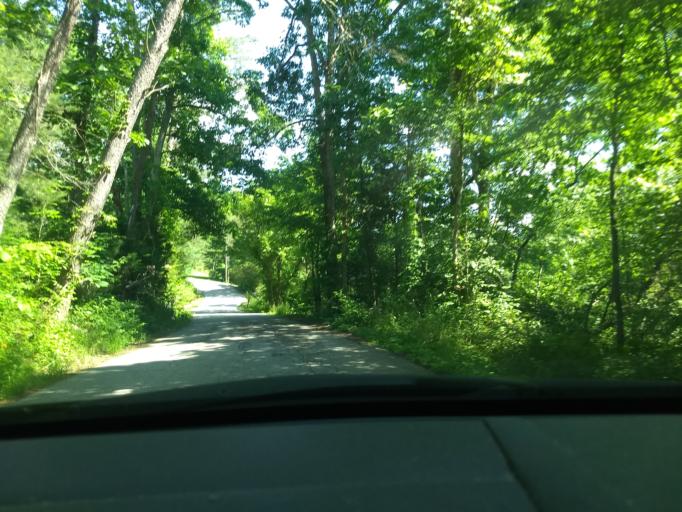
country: US
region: Indiana
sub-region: Floyd County
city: New Albany
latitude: 38.2634
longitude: -85.8630
